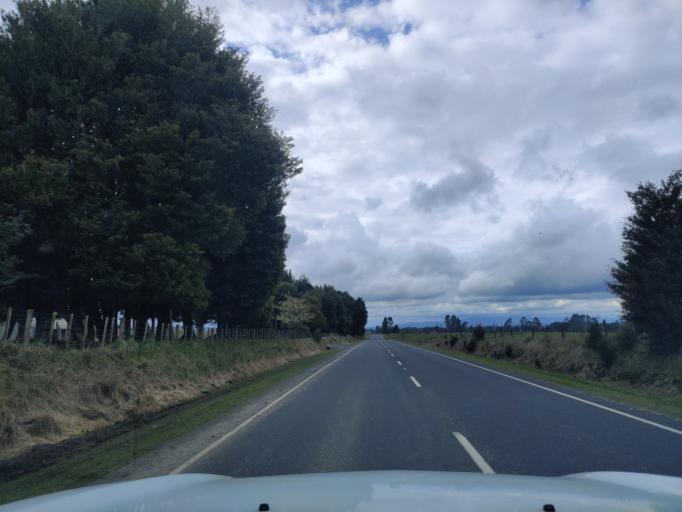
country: NZ
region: Waikato
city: Turangi
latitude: -39.0411
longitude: 175.3832
